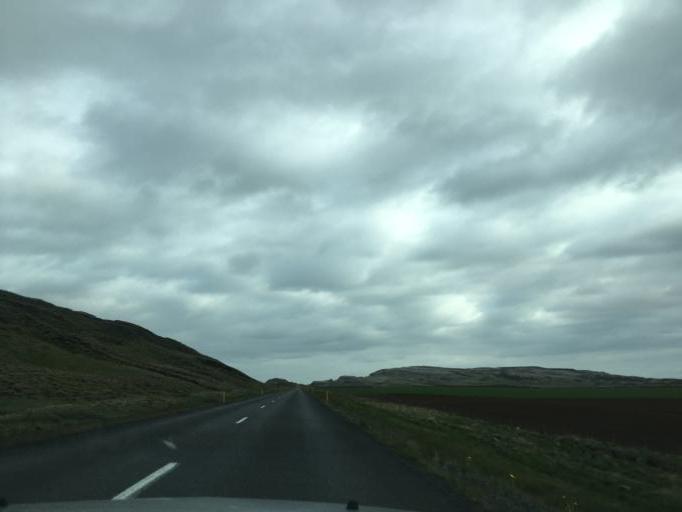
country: IS
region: South
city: Vestmannaeyjar
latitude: 64.2164
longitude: -20.2622
